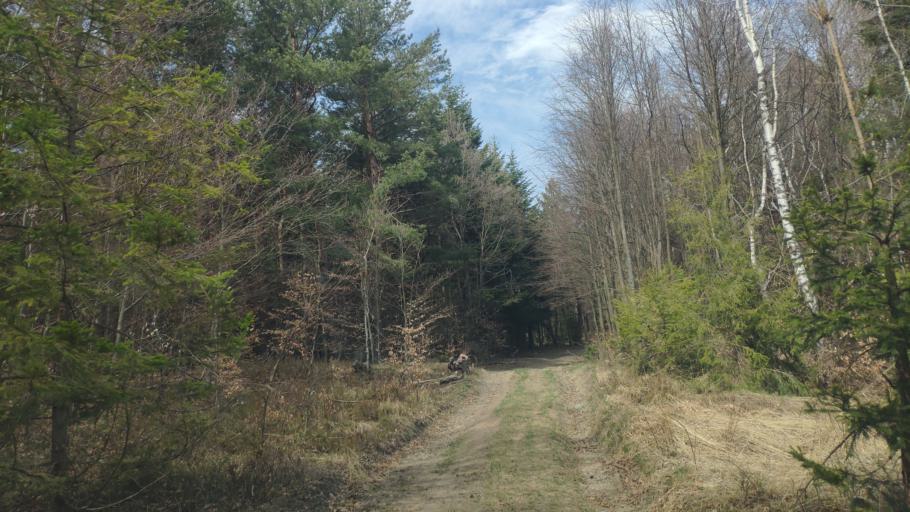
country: SK
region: Kosicky
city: Gelnica
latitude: 48.7534
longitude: 21.0207
